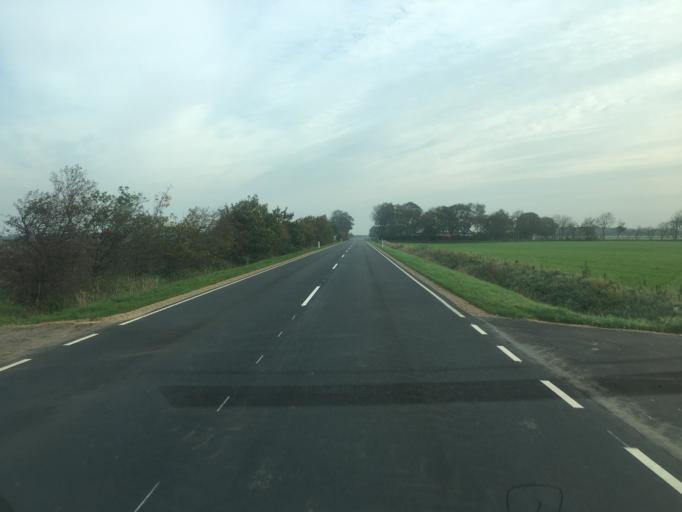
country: DK
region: South Denmark
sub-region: Tonder Kommune
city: Logumkloster
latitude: 55.0762
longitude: 8.9795
